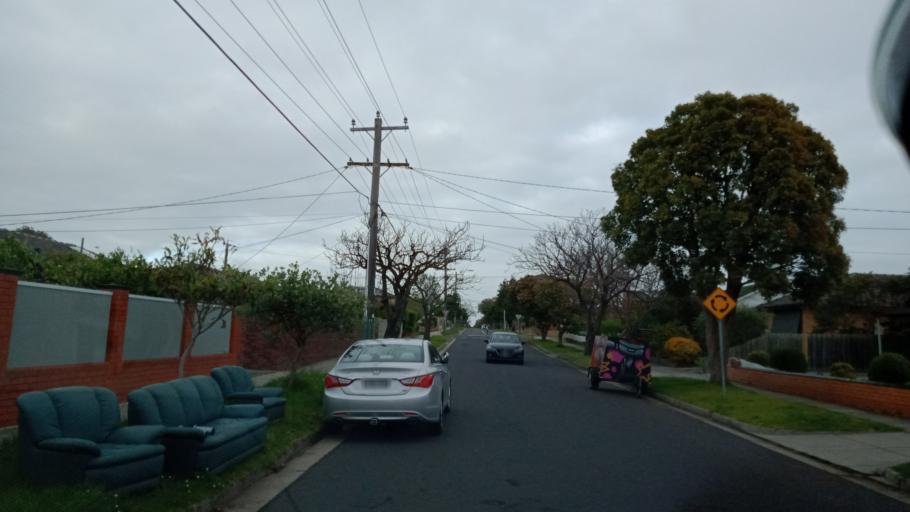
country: AU
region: Victoria
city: McKinnon
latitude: -37.9267
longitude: 145.0670
